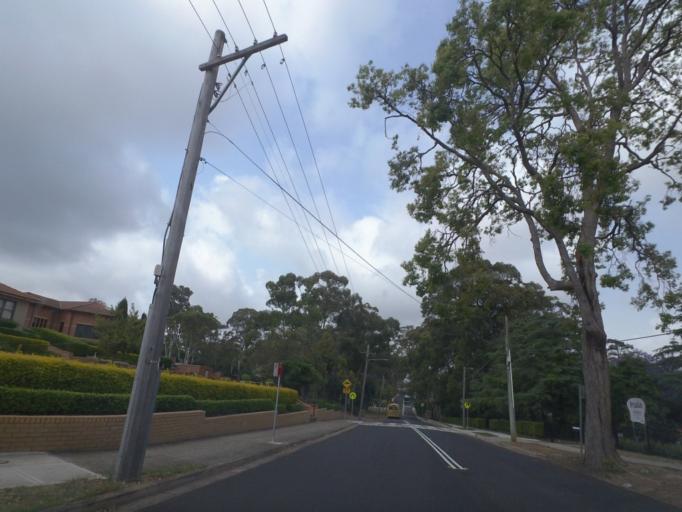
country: AU
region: New South Wales
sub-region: The Hills Shire
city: West Pennant
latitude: -33.7355
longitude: 151.0360
